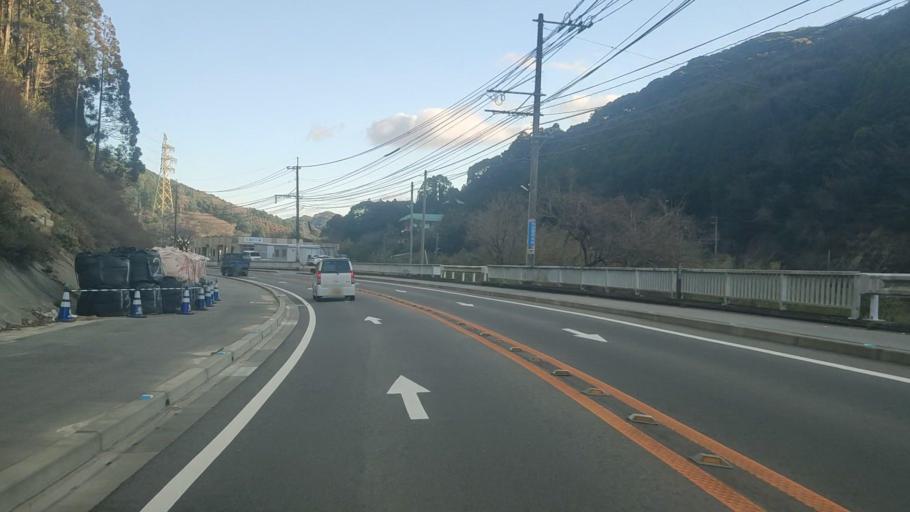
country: JP
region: Saga Prefecture
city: Saga-shi
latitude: 33.3324
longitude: 130.2634
